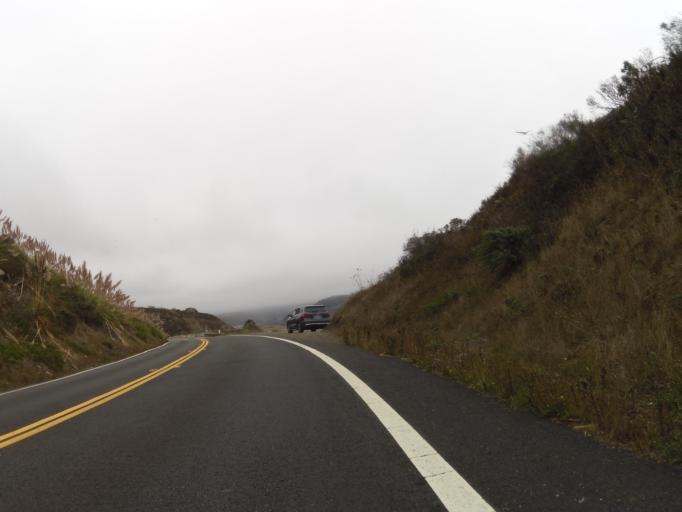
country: US
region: California
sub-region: Sonoma County
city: Monte Rio
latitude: 38.4560
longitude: -123.1364
